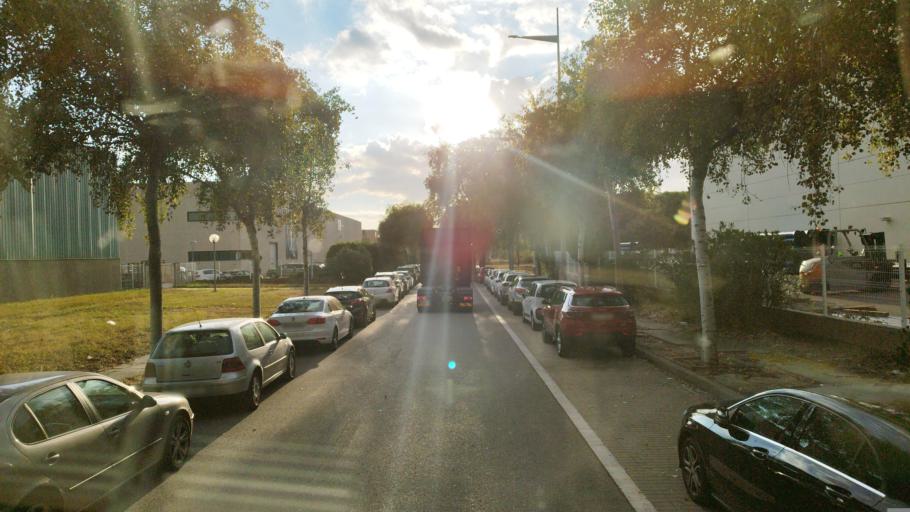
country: ES
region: Catalonia
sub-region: Provincia de Barcelona
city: Gava
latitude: 41.2857
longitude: 1.9937
